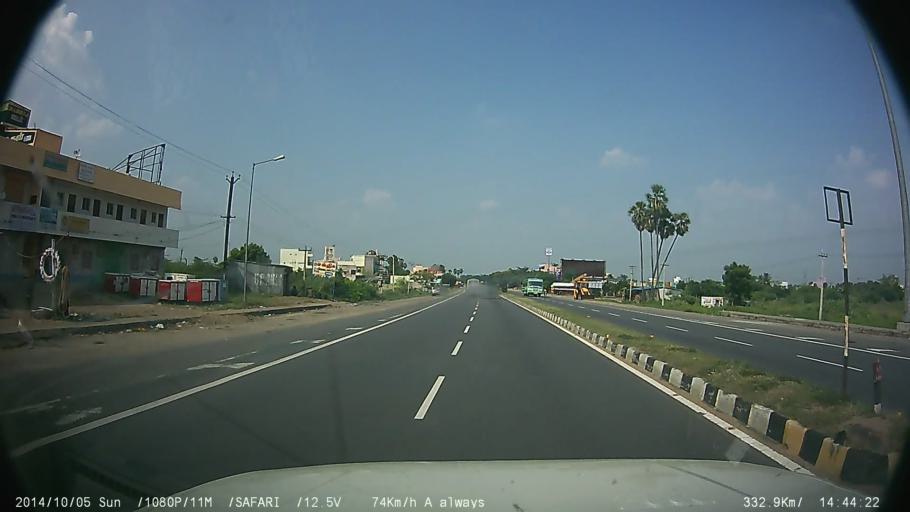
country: IN
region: Tamil Nadu
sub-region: Kancheepuram
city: Madurantakam
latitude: 12.4390
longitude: 79.8354
